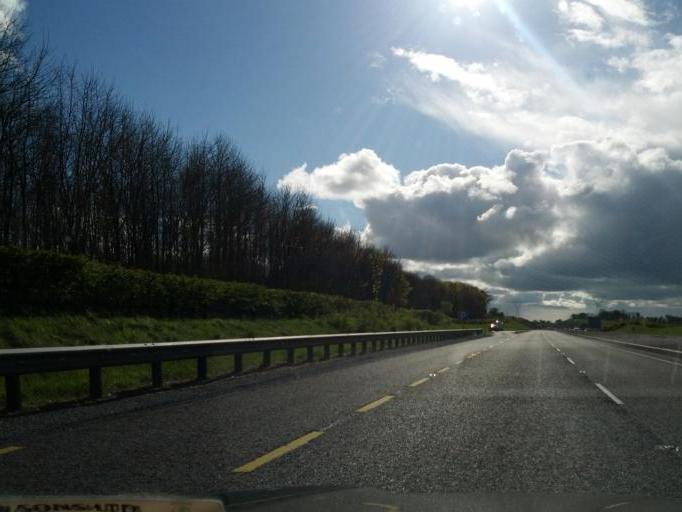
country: IE
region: Leinster
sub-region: An Iarmhi
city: Rochfortbridge
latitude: 53.3971
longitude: -7.3196
